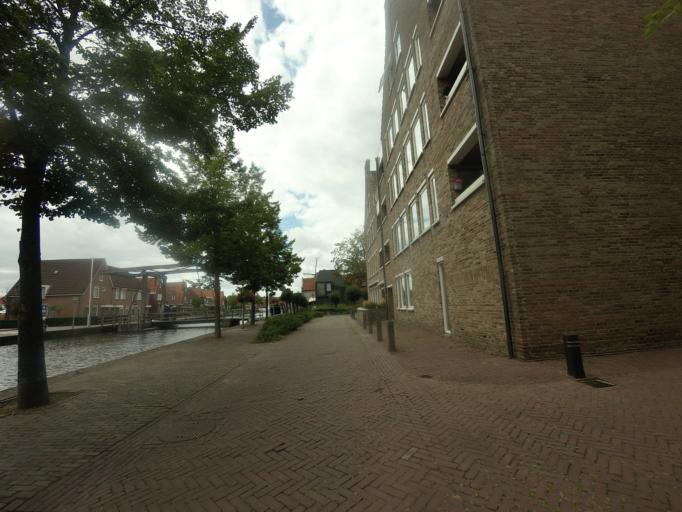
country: NL
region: Drenthe
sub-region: Gemeente Meppel
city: Meppel
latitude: 52.6955
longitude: 6.1889
